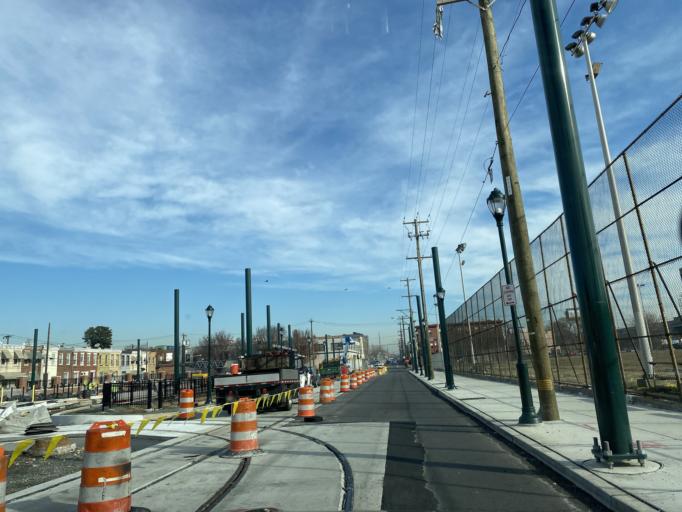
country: US
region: New Jersey
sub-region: Camden County
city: Merchantville
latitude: 39.9836
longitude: -75.1002
